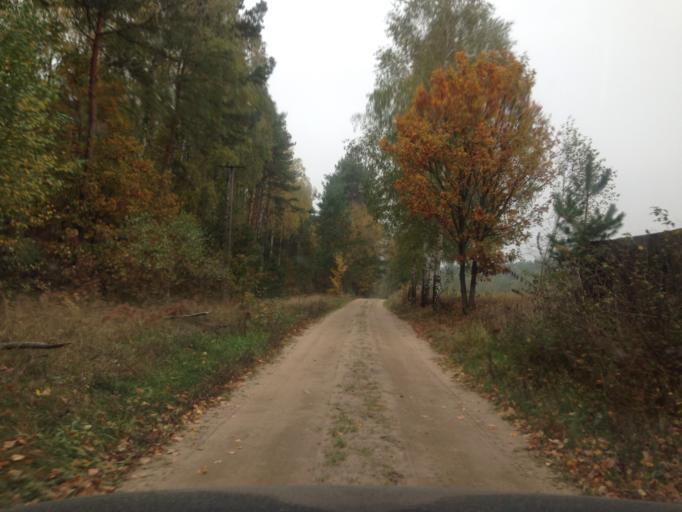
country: PL
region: Warmian-Masurian Voivodeship
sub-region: Powiat dzialdowski
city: Lidzbark
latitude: 53.2721
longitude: 19.7240
